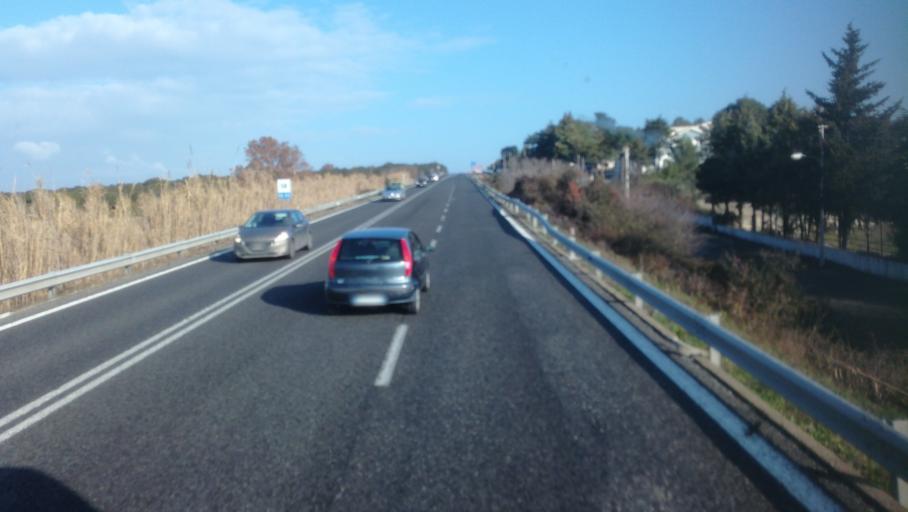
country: IT
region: Apulia
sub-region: Provincia di Taranto
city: Montemesola
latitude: 40.6283
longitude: 17.3161
